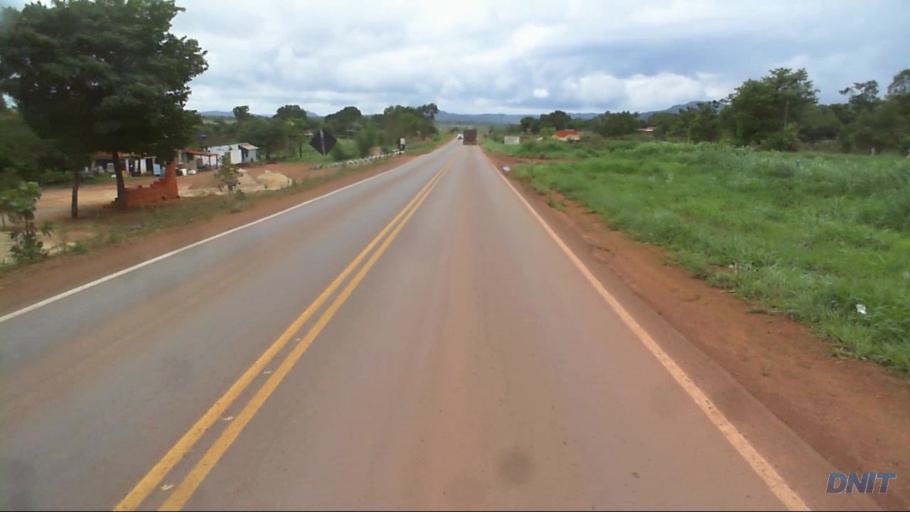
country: BR
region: Goias
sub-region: Padre Bernardo
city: Padre Bernardo
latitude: -15.3636
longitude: -48.2229
